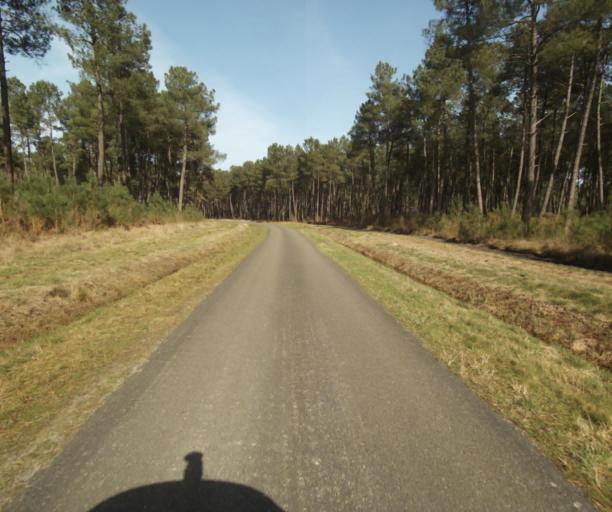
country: FR
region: Aquitaine
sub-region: Departement des Landes
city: Roquefort
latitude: 44.1839
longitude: -0.1899
